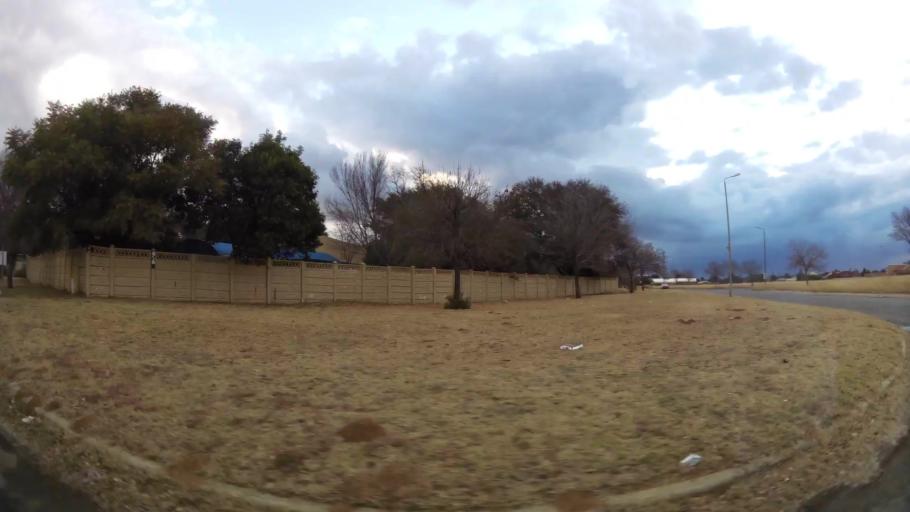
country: ZA
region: Orange Free State
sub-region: Lejweleputswa District Municipality
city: Welkom
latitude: -27.9541
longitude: 26.7409
